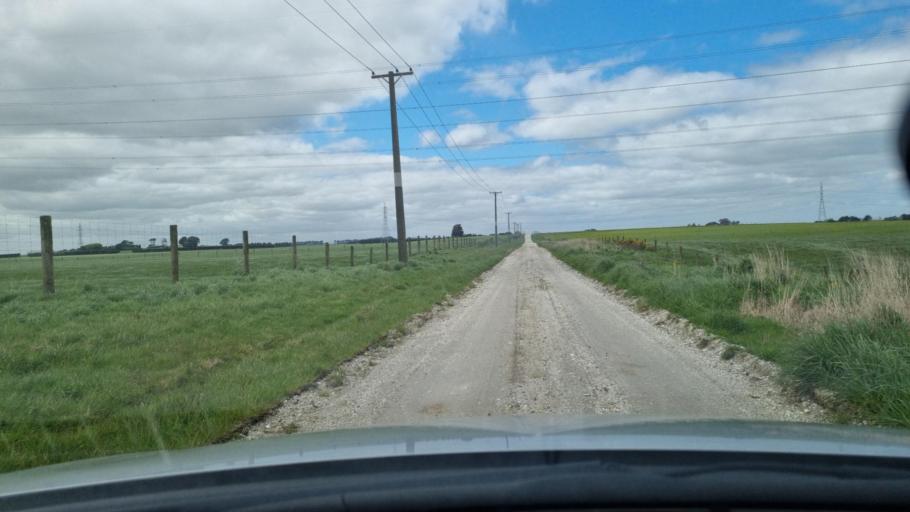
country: NZ
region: Southland
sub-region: Invercargill City
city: Invercargill
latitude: -46.4427
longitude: 168.4426
